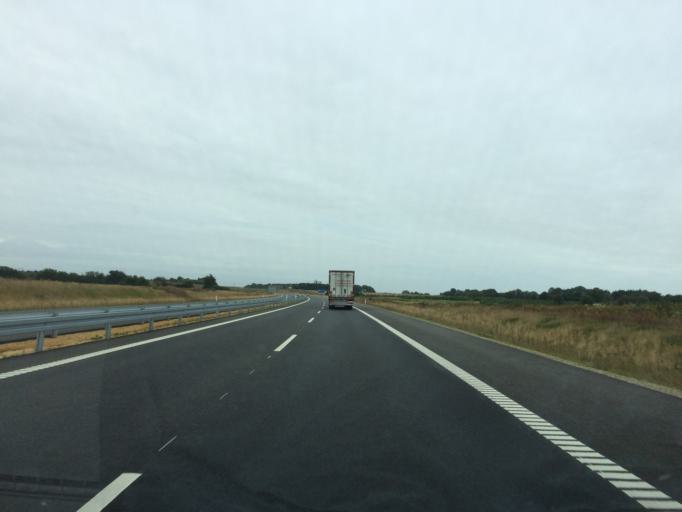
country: DK
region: Central Jutland
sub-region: Herning Kommune
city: Snejbjerg
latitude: 56.1446
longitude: 8.8696
